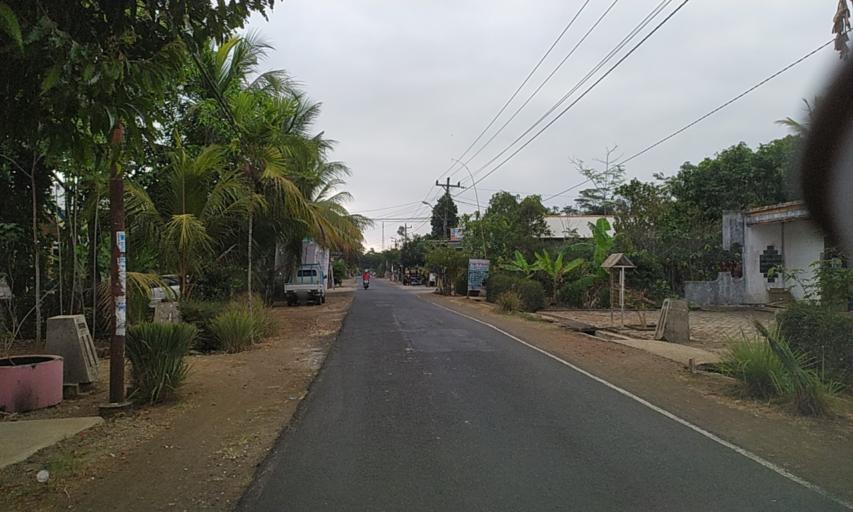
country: ID
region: Central Java
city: Kroya
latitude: -7.6658
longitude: 109.2481
